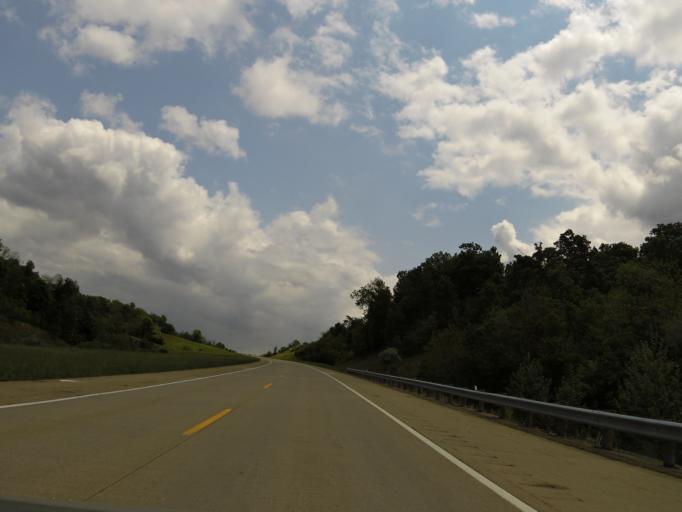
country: US
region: West Virginia
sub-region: Mason County
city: New Haven
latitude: 38.9996
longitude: -81.8842
